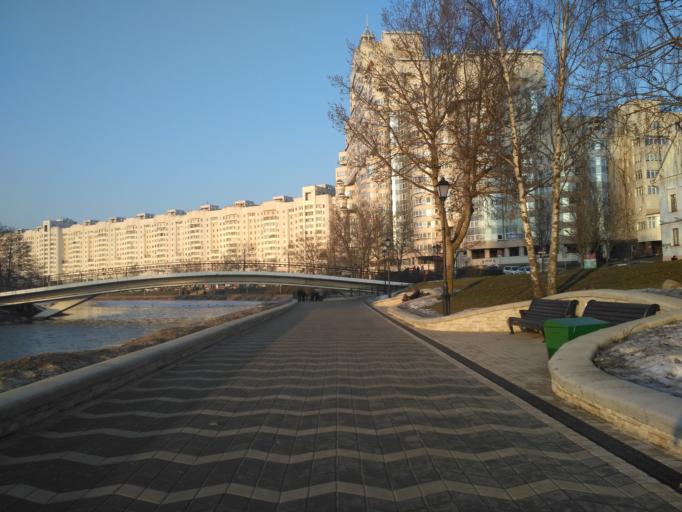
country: BY
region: Minsk
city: Minsk
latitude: 53.9091
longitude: 27.5553
